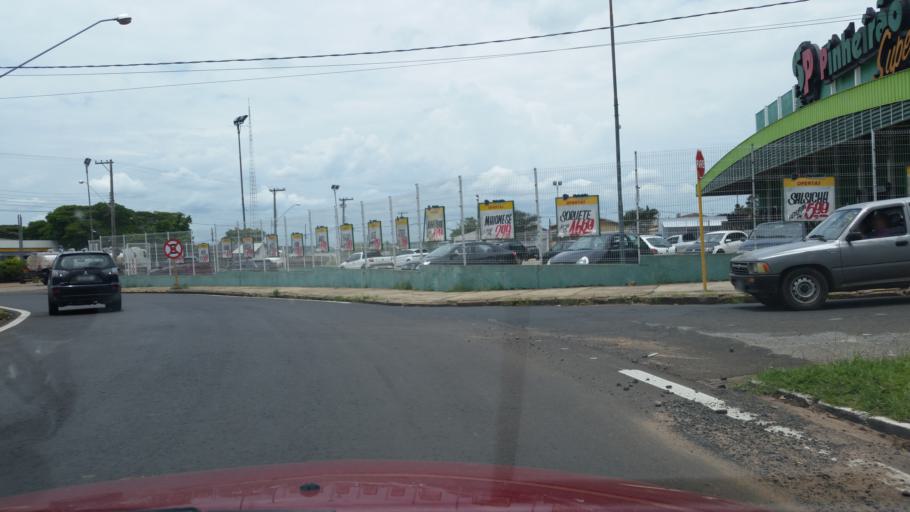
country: BR
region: Sao Paulo
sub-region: Avare
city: Avare
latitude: -23.0777
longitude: -48.9266
